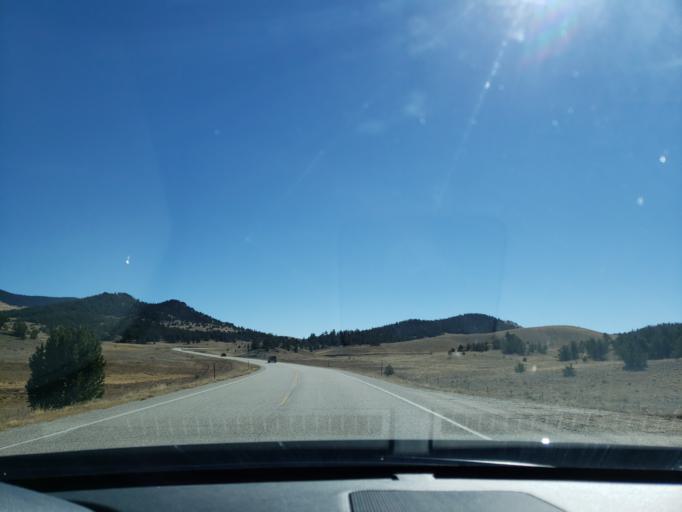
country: US
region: Colorado
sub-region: Chaffee County
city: Salida
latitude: 38.8497
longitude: -105.6502
